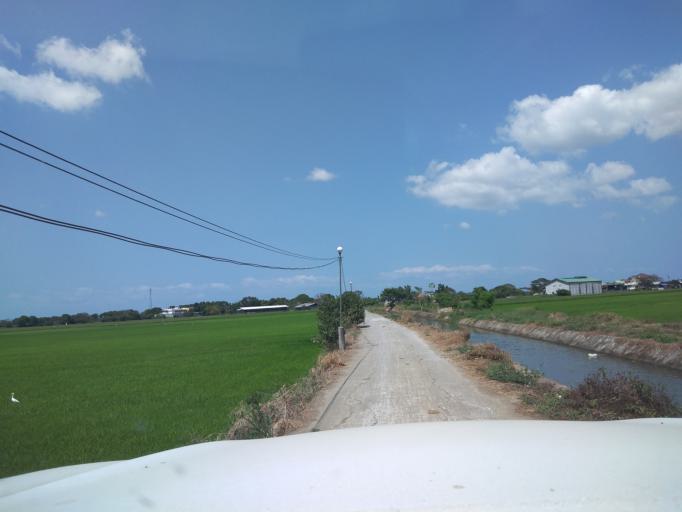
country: PH
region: Central Luzon
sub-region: Province of Pampanga
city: Bahay Pare
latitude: 15.0453
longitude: 120.8745
